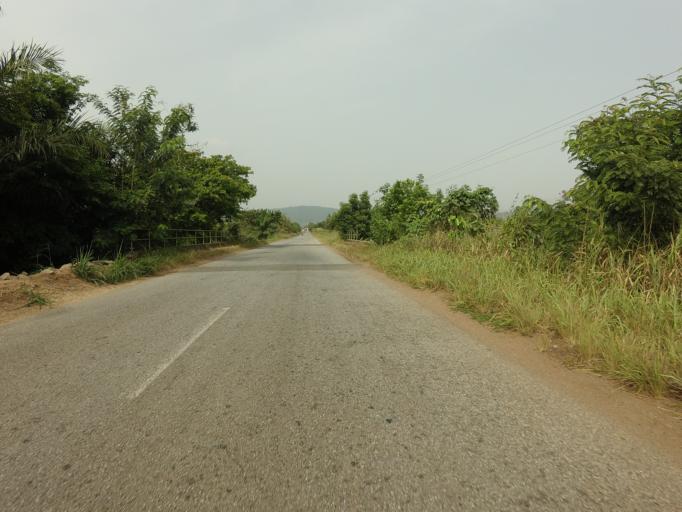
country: GH
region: Volta
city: Ho
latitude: 6.5749
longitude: 0.3386
